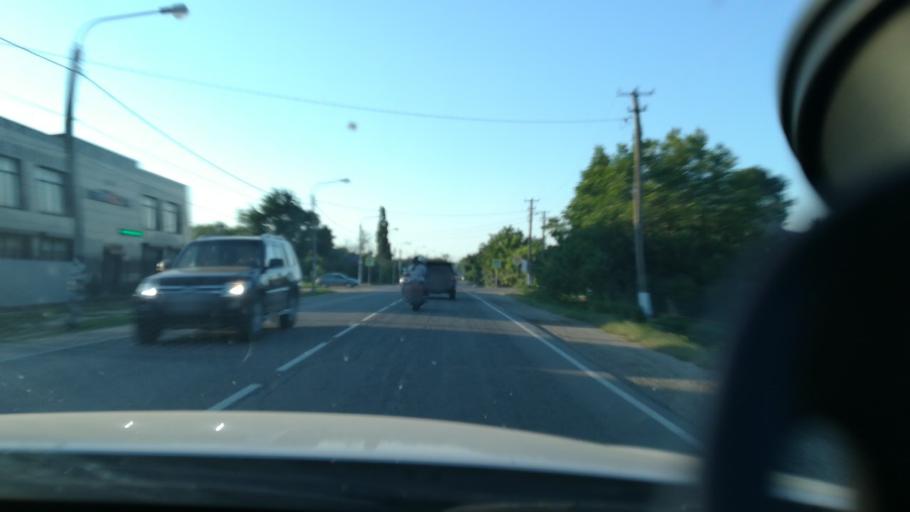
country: RU
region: Krasnodarskiy
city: Gostagayevskaya
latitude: 45.0177
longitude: 37.5022
